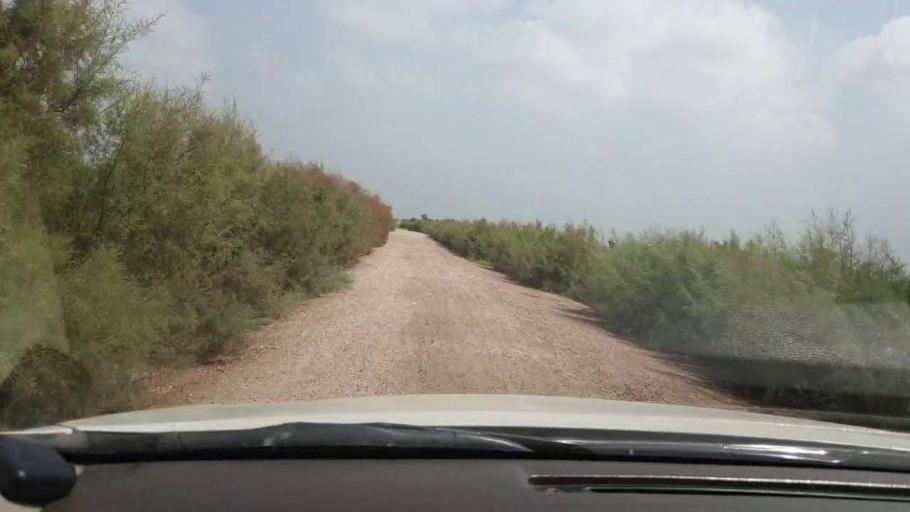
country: PK
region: Sindh
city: Garhi Yasin
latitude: 28.0079
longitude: 68.5397
